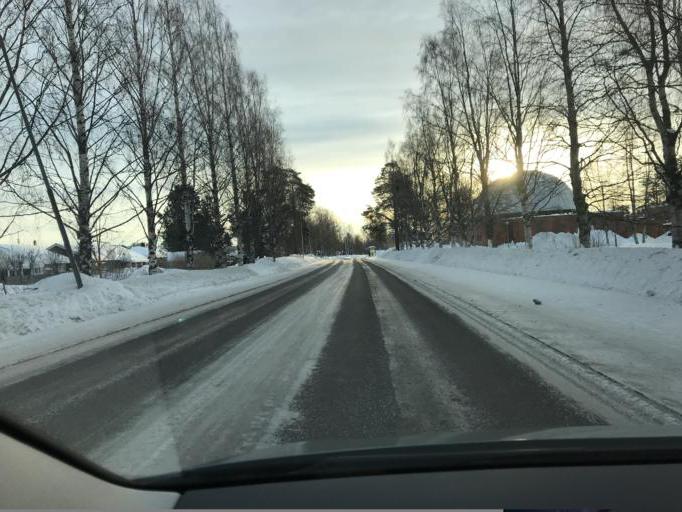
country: SE
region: Norrbotten
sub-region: Lulea Kommun
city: Bergnaset
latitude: 65.6046
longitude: 22.1166
